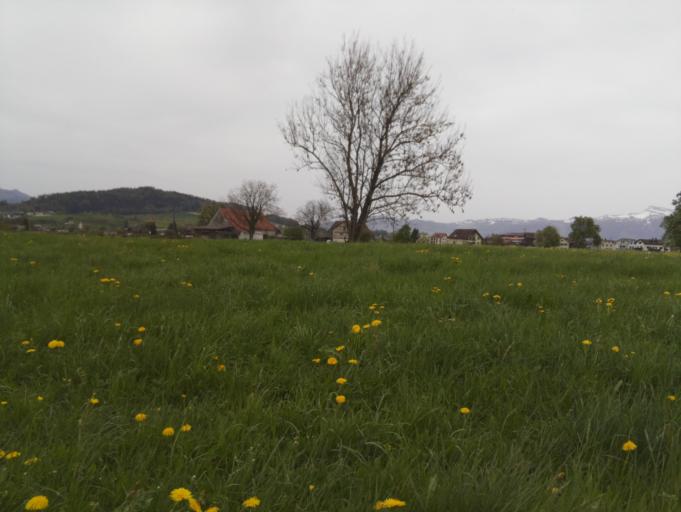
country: CH
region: Schwyz
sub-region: Bezirk March
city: Lachen
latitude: 47.1821
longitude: 8.8851
